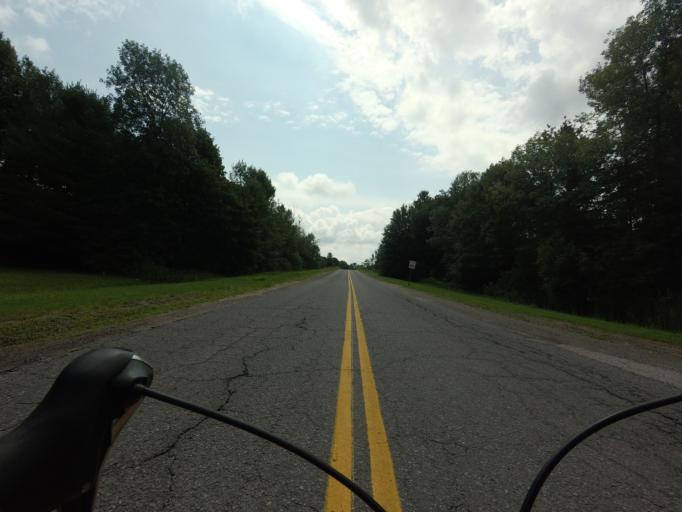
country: CA
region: Ontario
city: Brockville
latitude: 44.6276
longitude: -75.6633
